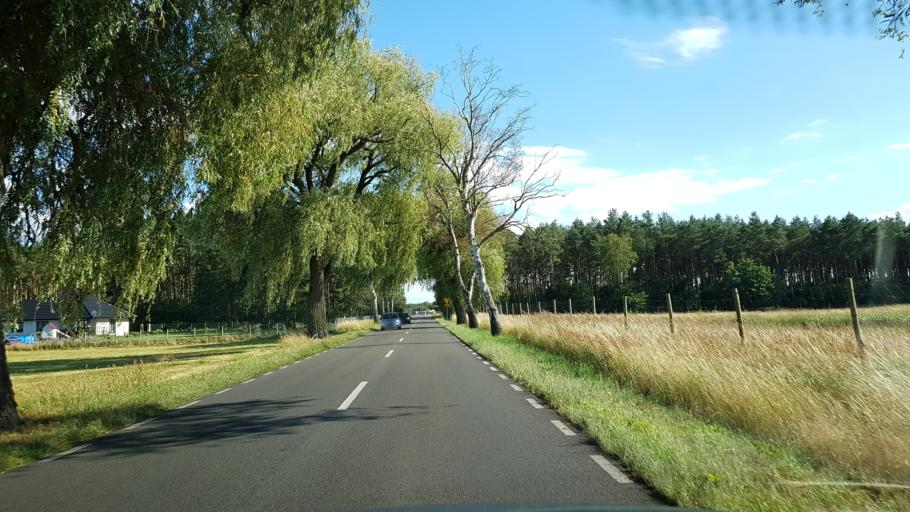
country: PL
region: West Pomeranian Voivodeship
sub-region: Powiat goleniowski
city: Goleniow
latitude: 53.5816
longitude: 14.7408
